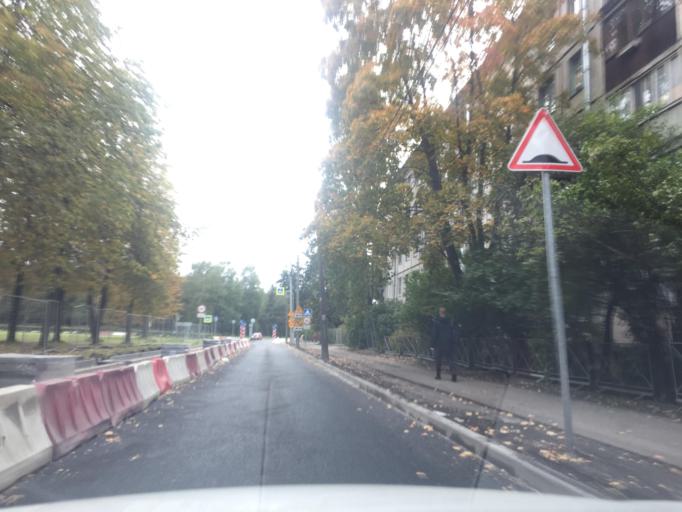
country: RU
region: Leningrad
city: Akademicheskoe
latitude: 60.0056
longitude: 30.4212
